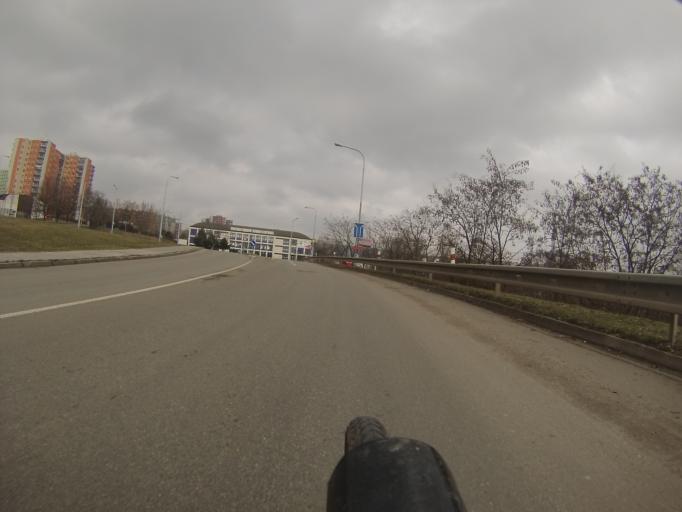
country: CZ
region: South Moravian
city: Bilovice nad Svitavou
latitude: 49.1996
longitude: 16.6636
